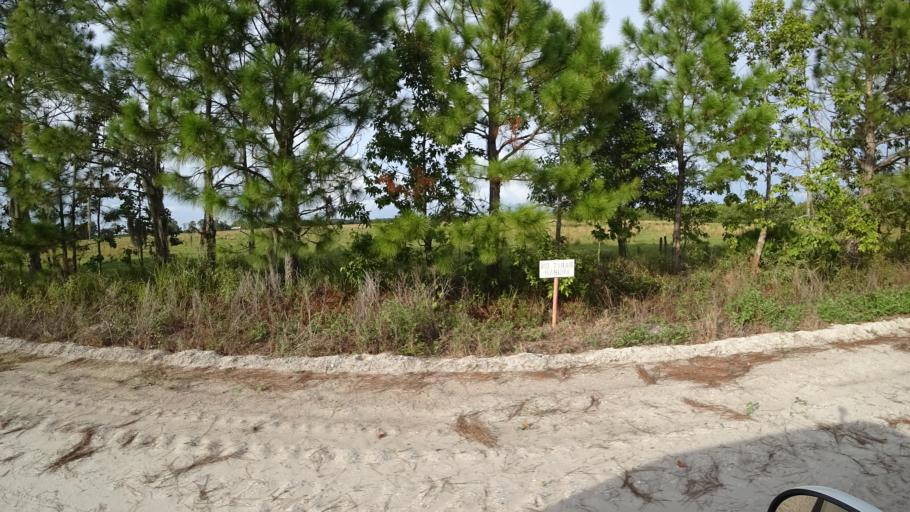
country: US
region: Florida
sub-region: Hillsborough County
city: Wimauma
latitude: 27.5664
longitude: -82.0845
